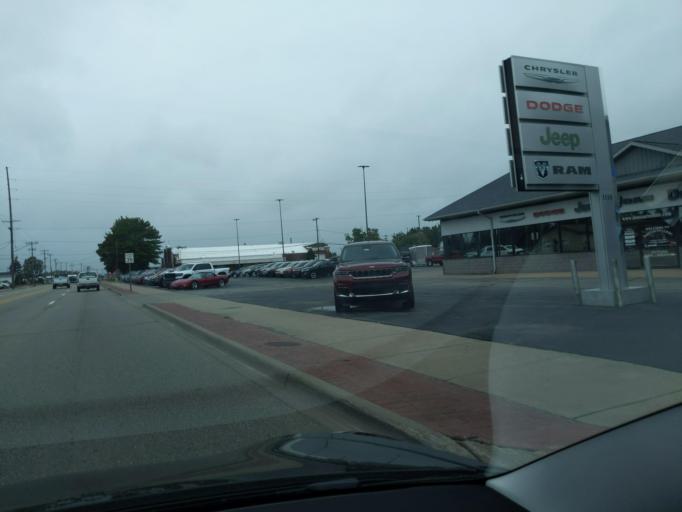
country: US
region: Michigan
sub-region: Wexford County
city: Cadillac
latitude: 44.2637
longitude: -85.4058
